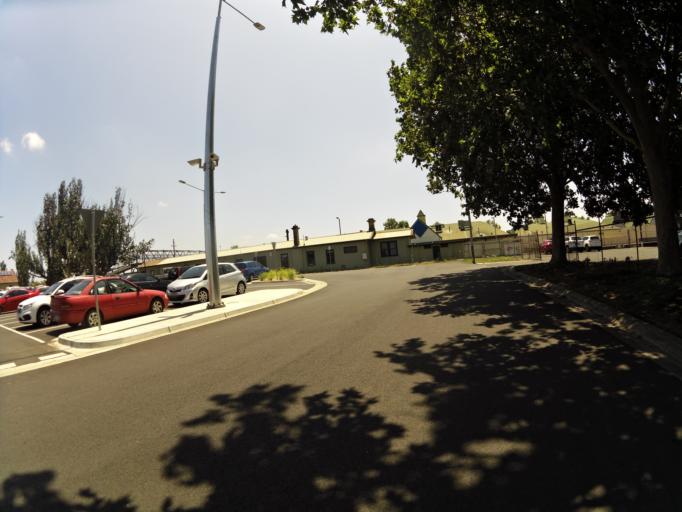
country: AU
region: Victoria
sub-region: Latrobe
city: Traralgon
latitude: -38.1991
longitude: 146.5390
